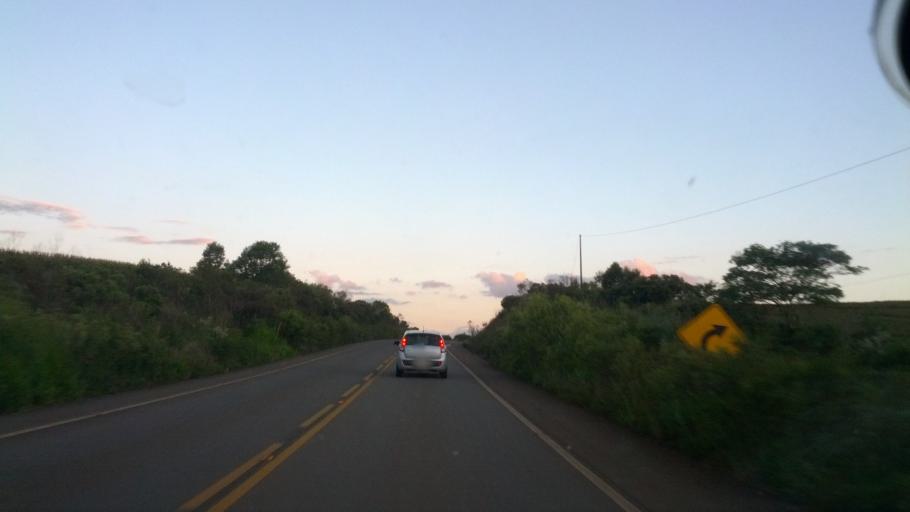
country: BR
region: Rio Grande do Sul
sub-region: Vacaria
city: Estrela
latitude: -27.8781
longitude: -50.7985
